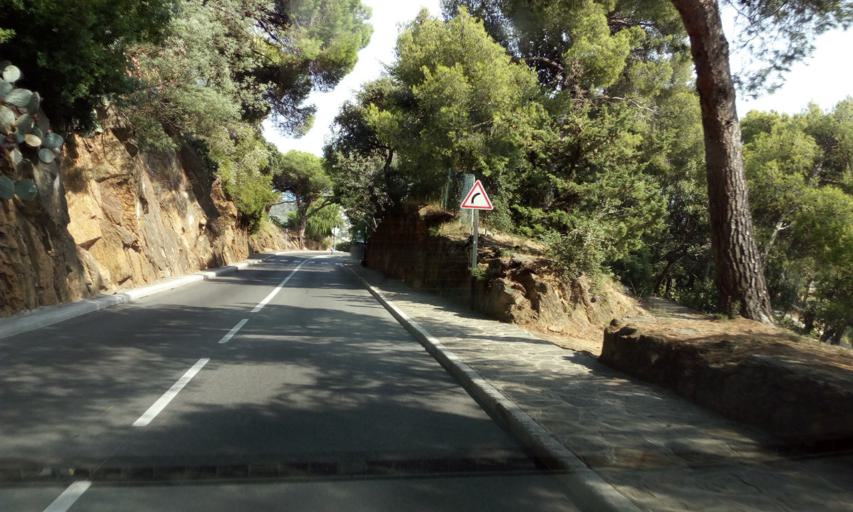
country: FR
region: Provence-Alpes-Cote d'Azur
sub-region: Departement du Var
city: Bormes-les-Mimosas
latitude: 43.1496
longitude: 6.3460
